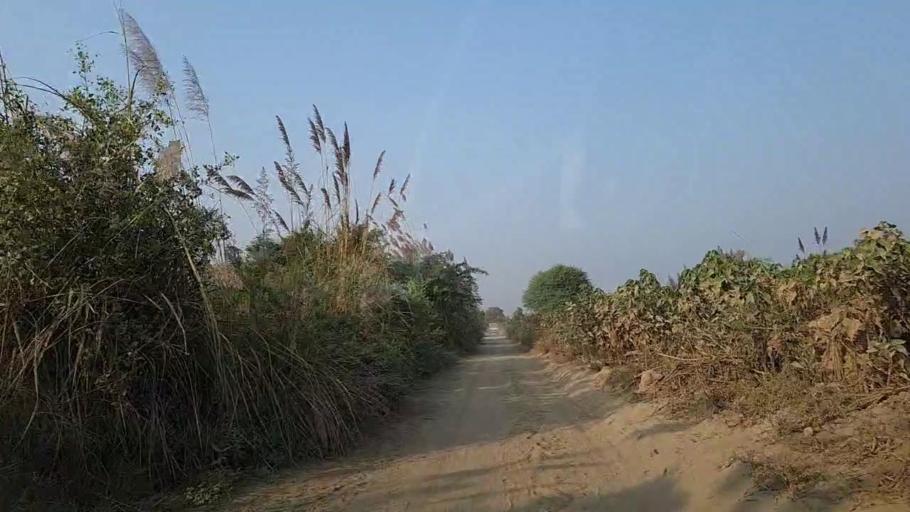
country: PK
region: Sindh
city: Thatta
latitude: 24.6775
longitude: 67.7840
